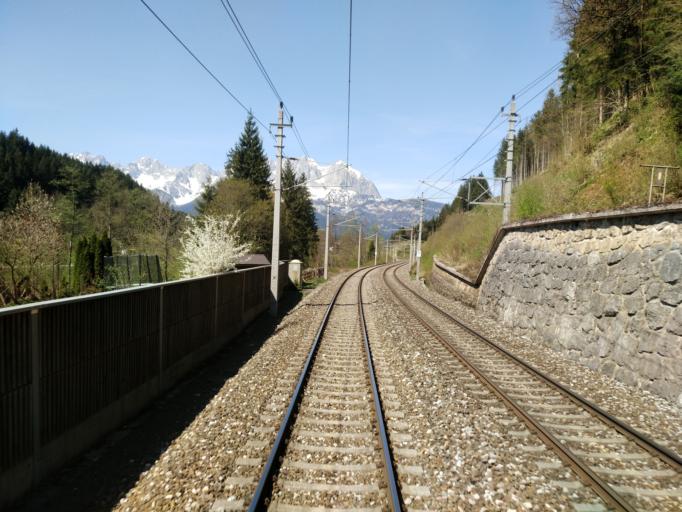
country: AT
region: Tyrol
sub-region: Politischer Bezirk Kitzbuhel
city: Oberndorf in Tirol
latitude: 47.4735
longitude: 12.3856
